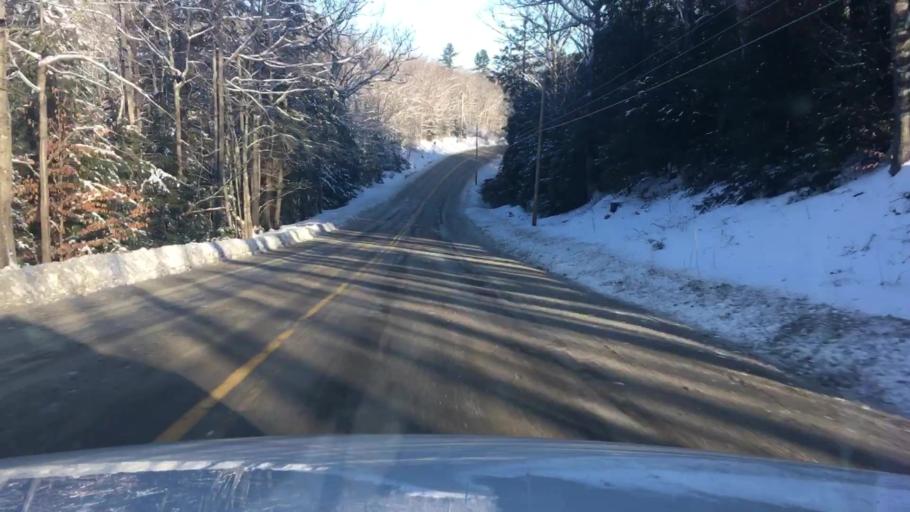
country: US
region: Maine
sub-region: Kennebec County
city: Mount Vernon
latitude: 44.4672
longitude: -69.9741
